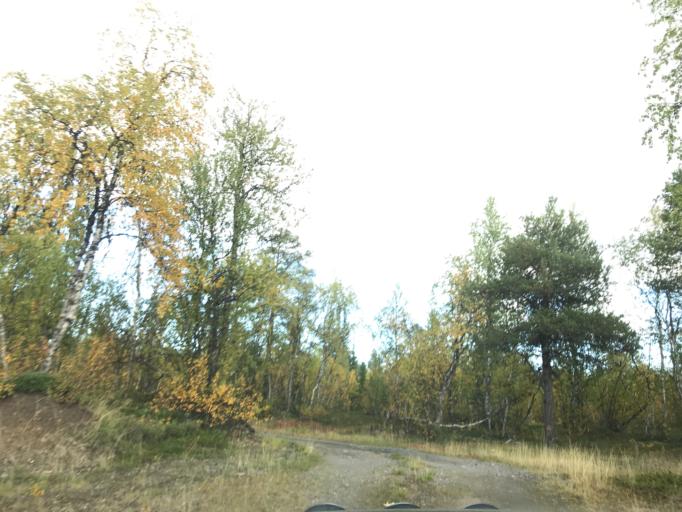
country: SE
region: Norrbotten
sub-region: Gallivare Kommun
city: Malmberget
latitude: 67.5839
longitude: 20.8543
